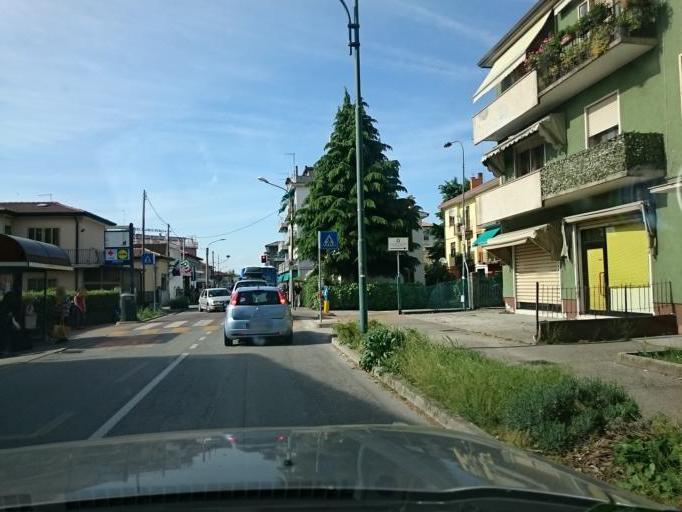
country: IT
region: Veneto
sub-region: Provincia di Venezia
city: Campalto
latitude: 45.4860
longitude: 12.2958
